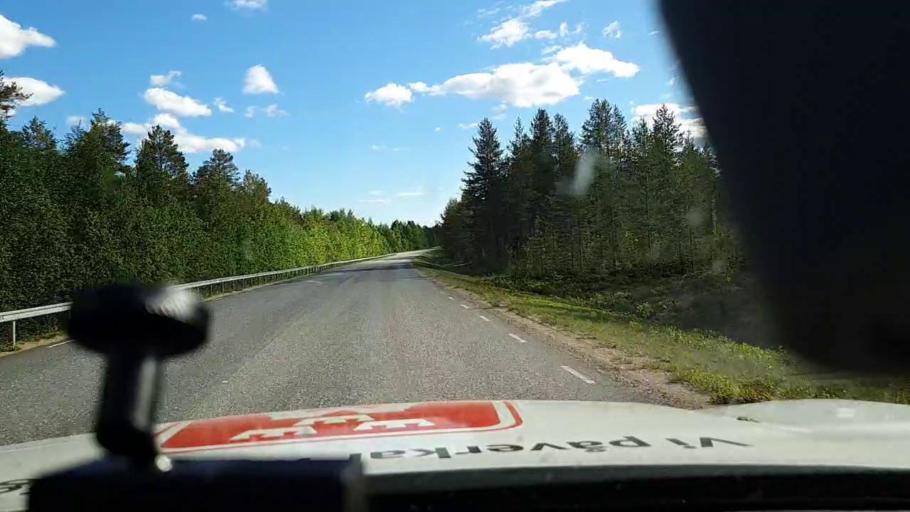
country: SE
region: Norrbotten
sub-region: Overtornea Kommun
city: OEvertornea
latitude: 66.3454
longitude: 23.6483
